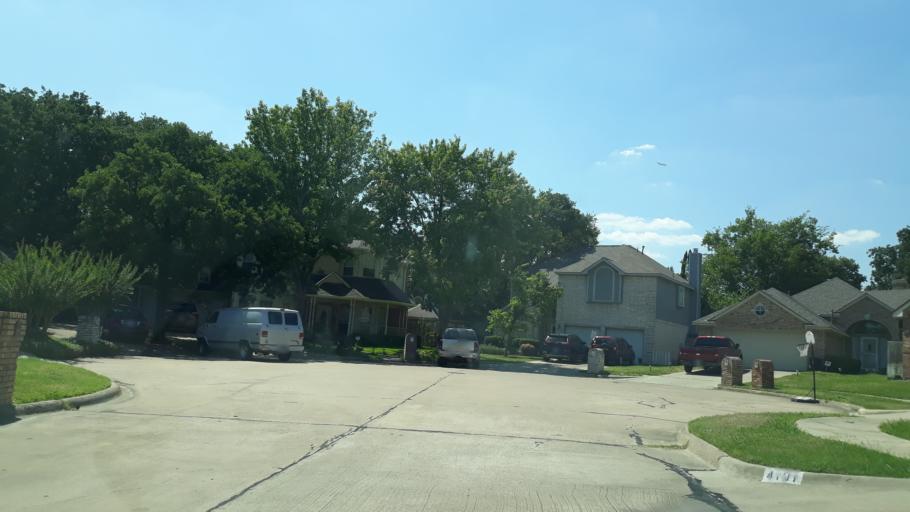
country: US
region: Texas
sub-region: Dallas County
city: Irving
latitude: 32.8298
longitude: -97.0046
